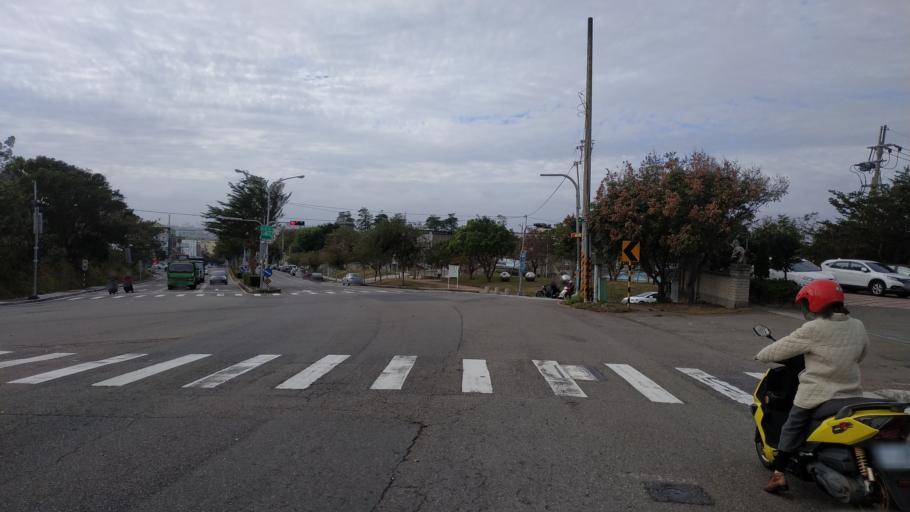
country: TW
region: Taiwan
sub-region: Taichung City
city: Taichung
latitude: 24.2324
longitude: 120.5655
